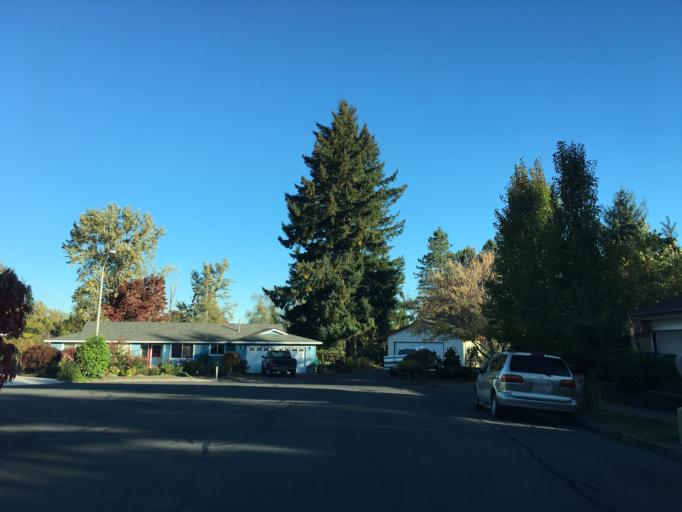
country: US
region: Oregon
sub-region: Multnomah County
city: Wood Village
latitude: 45.5097
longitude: -122.4032
